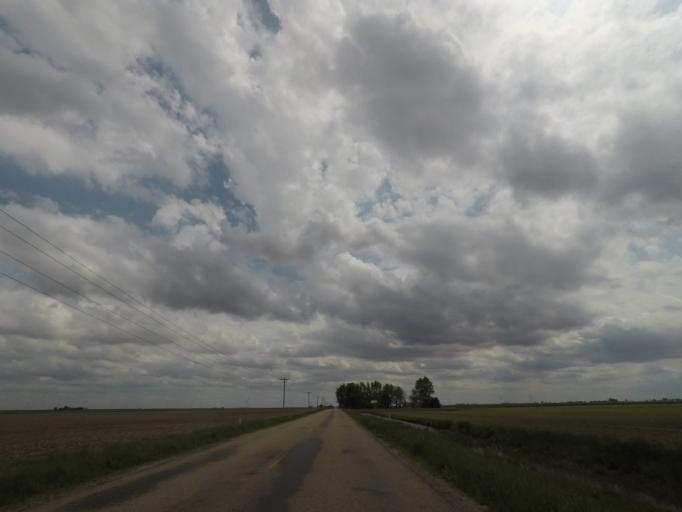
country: US
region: Illinois
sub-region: De Witt County
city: Clinton
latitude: 40.0888
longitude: -89.0859
